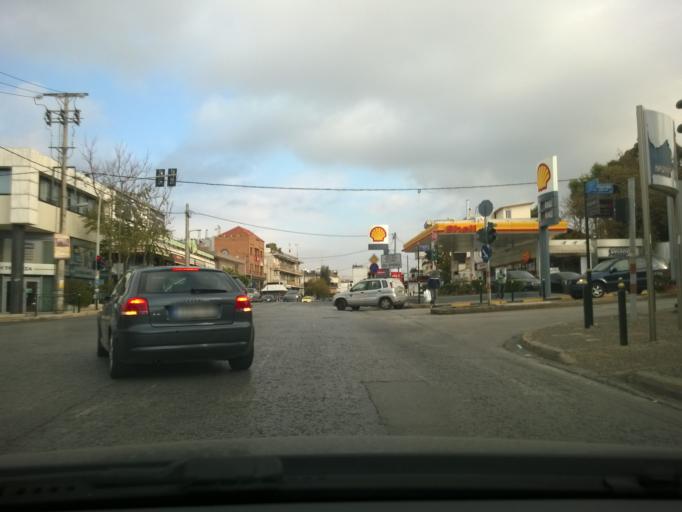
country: GR
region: Attica
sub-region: Nomarchia Athinas
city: Nea Erythraia
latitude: 38.0878
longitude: 23.8174
